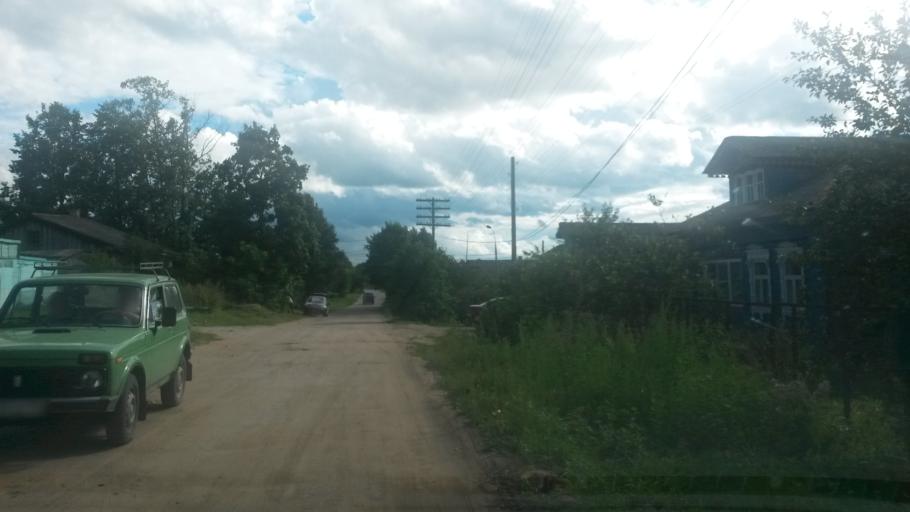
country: RU
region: Jaroslavl
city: Petrovsk
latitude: 57.0143
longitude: 39.2600
